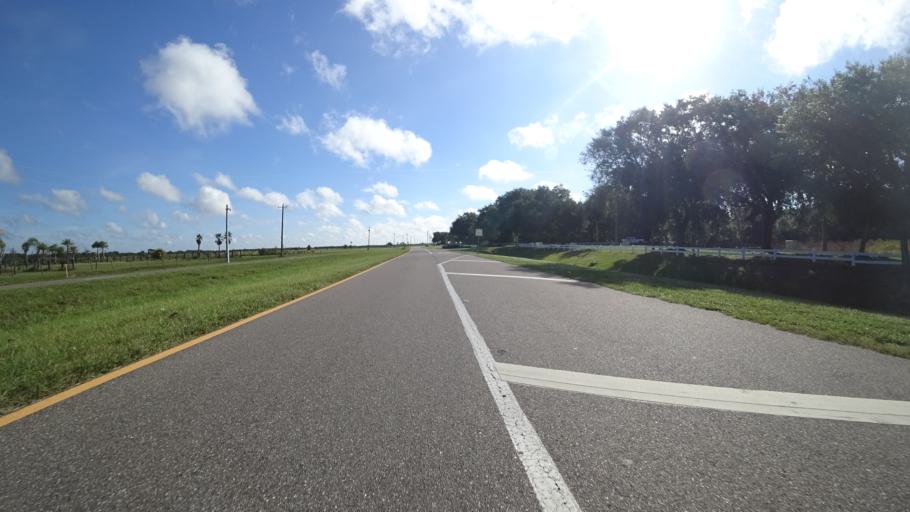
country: US
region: Florida
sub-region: Manatee County
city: Ellenton
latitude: 27.6011
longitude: -82.4940
